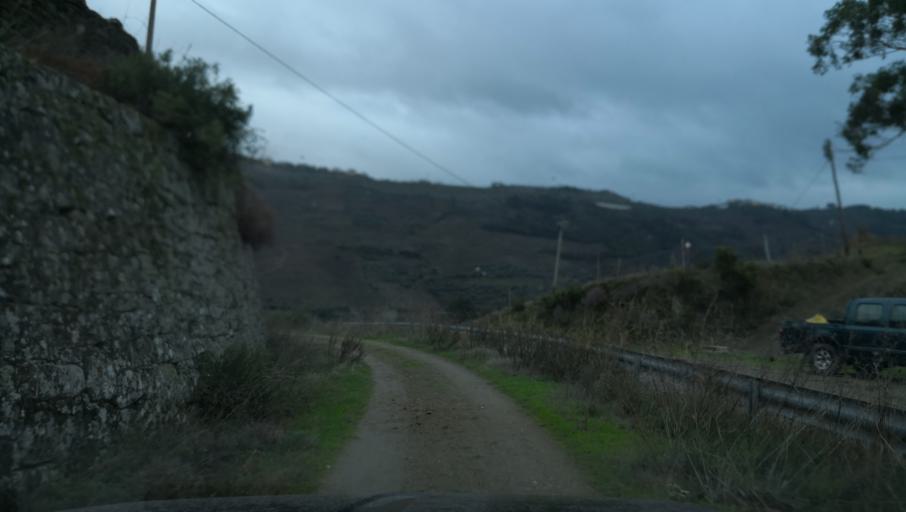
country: PT
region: Vila Real
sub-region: Santa Marta de Penaguiao
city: Santa Marta de Penaguiao
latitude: 41.2370
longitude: -7.7463
